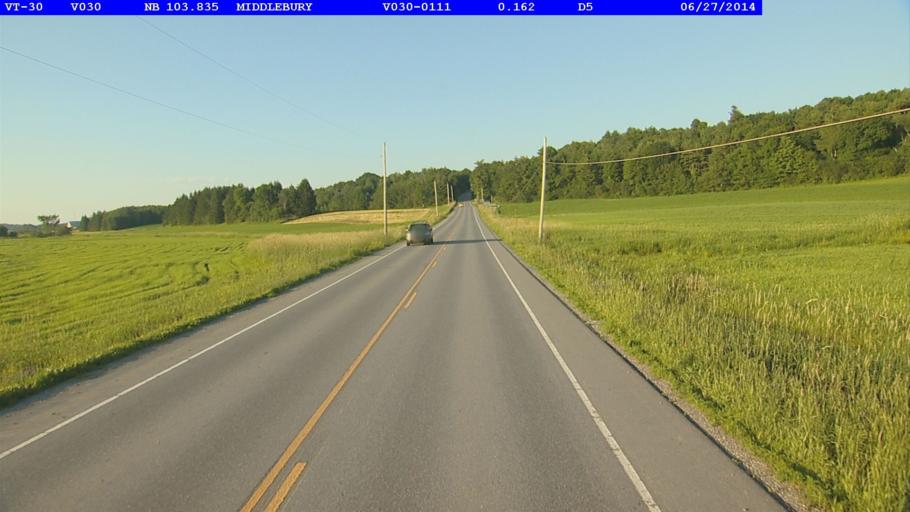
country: US
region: Vermont
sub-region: Addison County
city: Middlebury (village)
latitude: 43.9971
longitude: -73.1880
